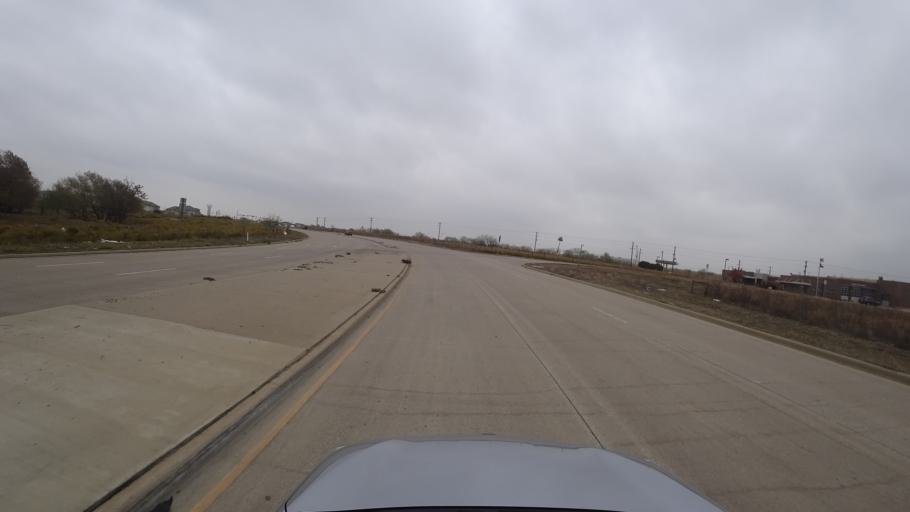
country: US
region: Texas
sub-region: Denton County
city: The Colony
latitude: 33.0479
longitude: -96.9268
